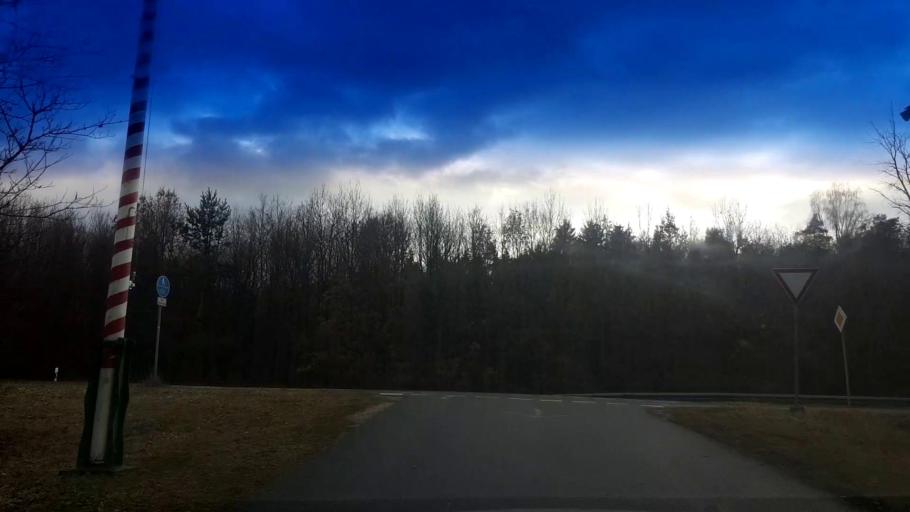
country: DE
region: Bavaria
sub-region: Upper Franconia
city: Litzendorf
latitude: 49.8879
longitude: 10.9814
